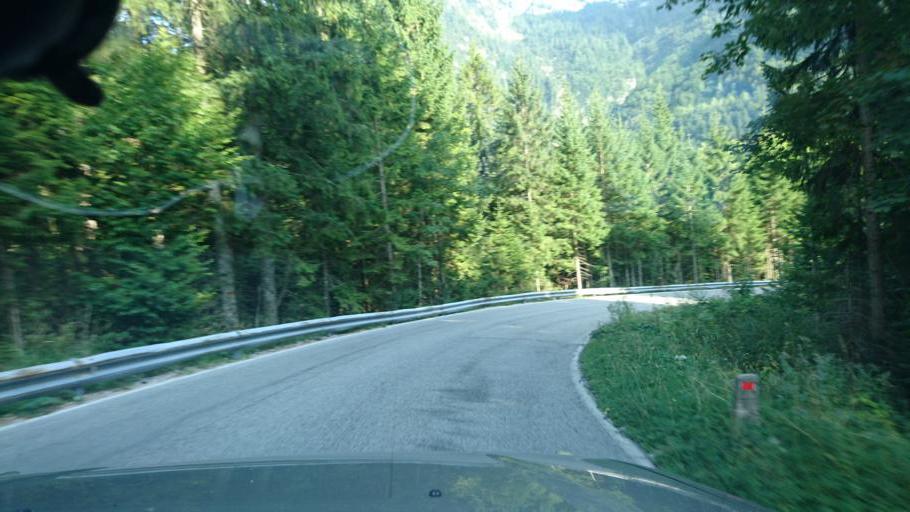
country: SI
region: Bovec
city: Bovec
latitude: 46.3961
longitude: 13.4956
